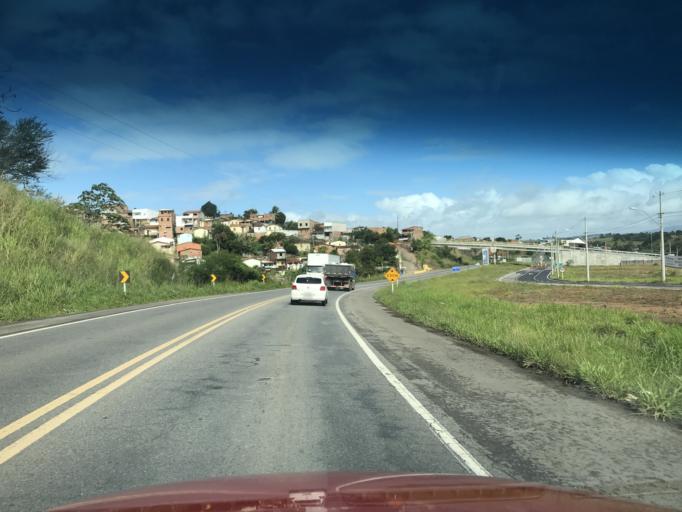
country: BR
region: Bahia
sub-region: Santo Antonio De Jesus
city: Santo Antonio de Jesus
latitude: -12.9551
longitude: -39.2575
